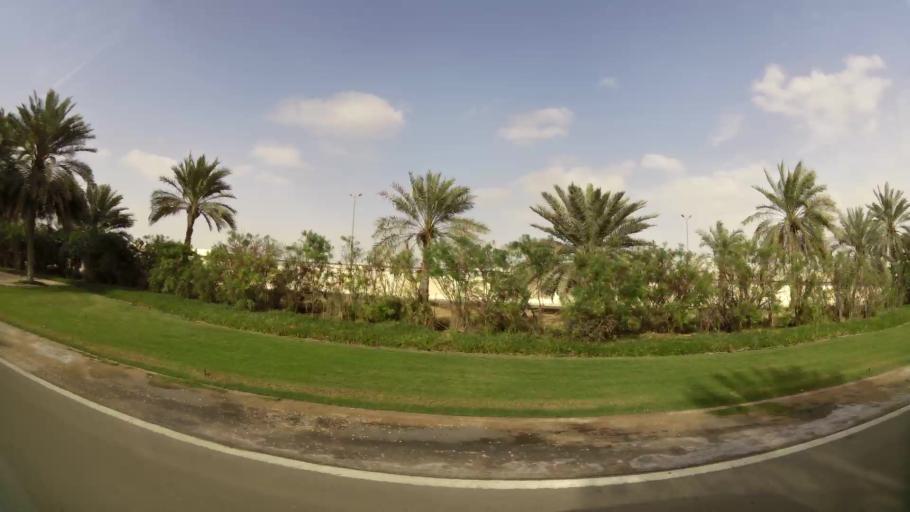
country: AE
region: Abu Dhabi
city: Abu Dhabi
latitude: 24.4359
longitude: 54.6253
